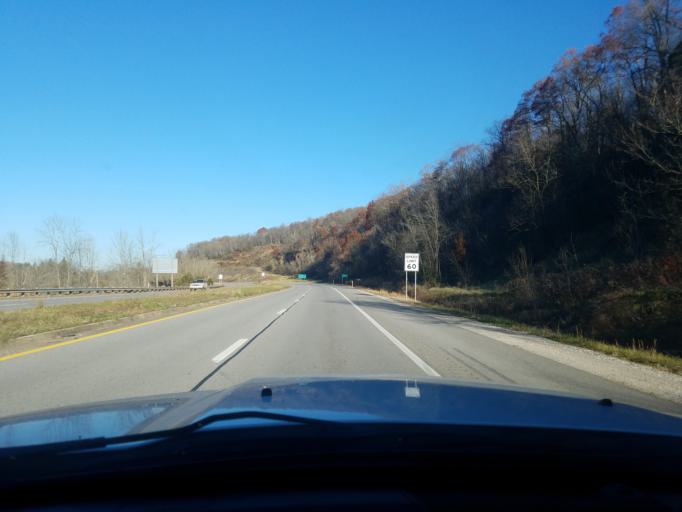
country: US
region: West Virginia
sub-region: Jackson County
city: Ravenswood
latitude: 38.9272
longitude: -81.7228
